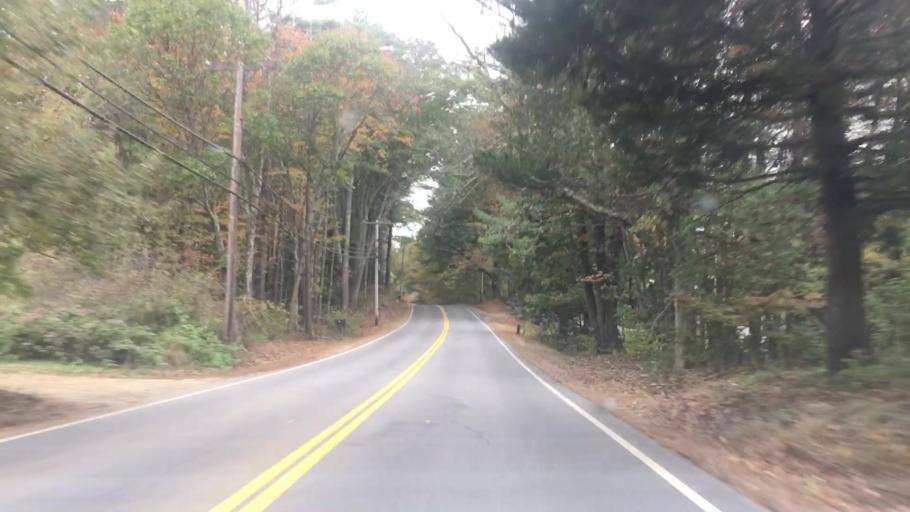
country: US
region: New Hampshire
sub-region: Rockingham County
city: Exeter
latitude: 42.9878
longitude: -70.9968
